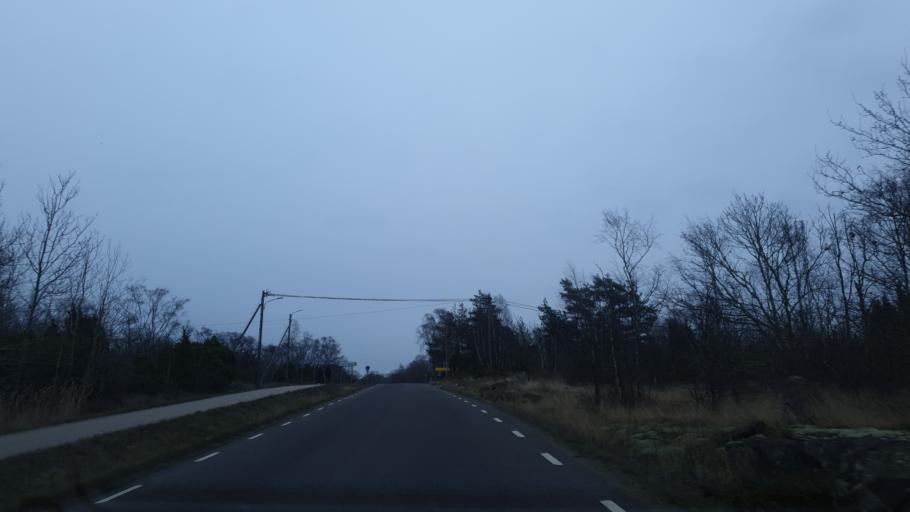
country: SE
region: Blekinge
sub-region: Karlskrona Kommun
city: Sturko
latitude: 56.1145
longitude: 15.6587
